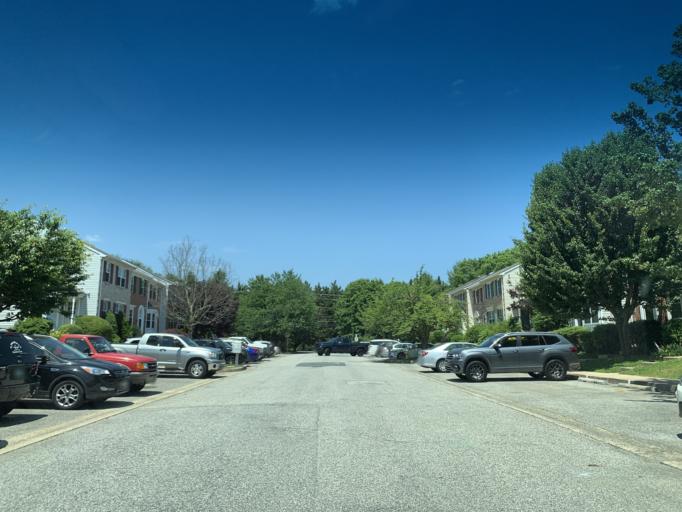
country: US
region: Maryland
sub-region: Harford County
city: Bel Air North
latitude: 39.5746
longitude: -76.3602
